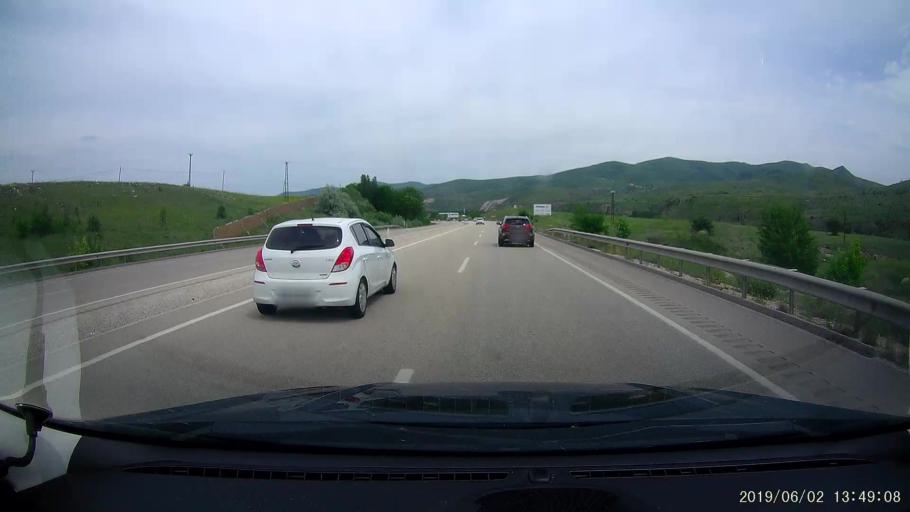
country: TR
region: Cankiri
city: Kursunlu
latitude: 40.8312
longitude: 33.3218
